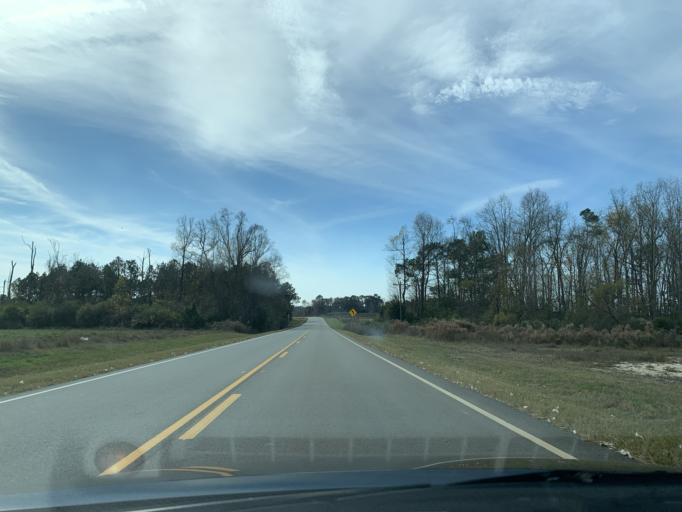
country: US
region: Georgia
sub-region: Turner County
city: Ashburn
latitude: 31.7462
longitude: -83.5653
